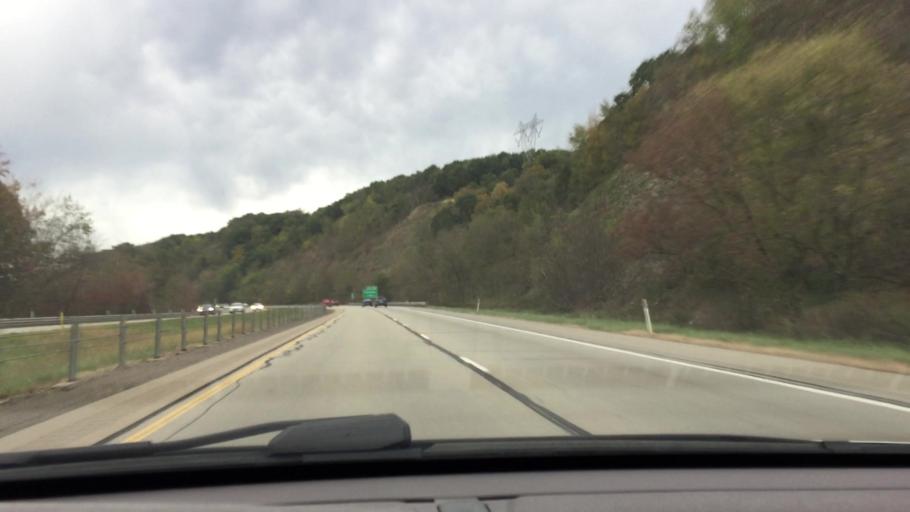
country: US
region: Pennsylvania
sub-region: Beaver County
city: Beaver
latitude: 40.6161
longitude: -80.3203
